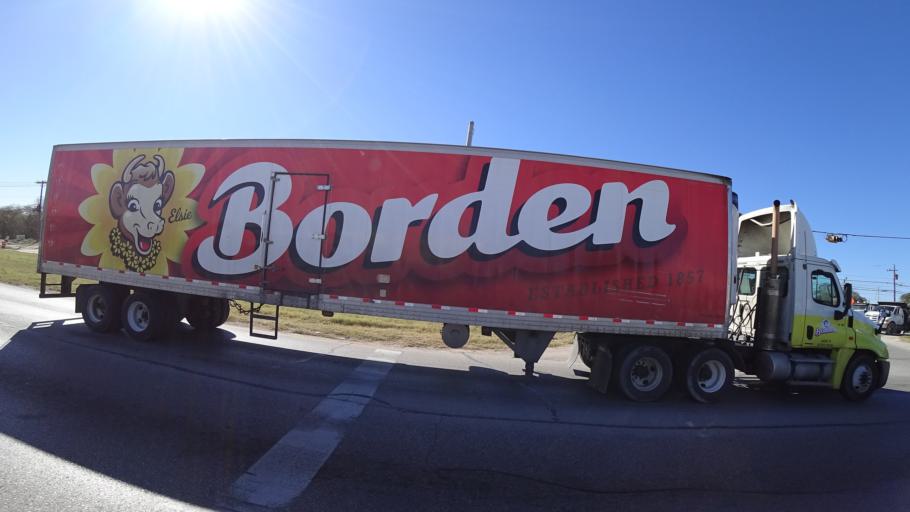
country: US
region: Texas
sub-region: Travis County
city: Austin
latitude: 30.2364
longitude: -97.6860
